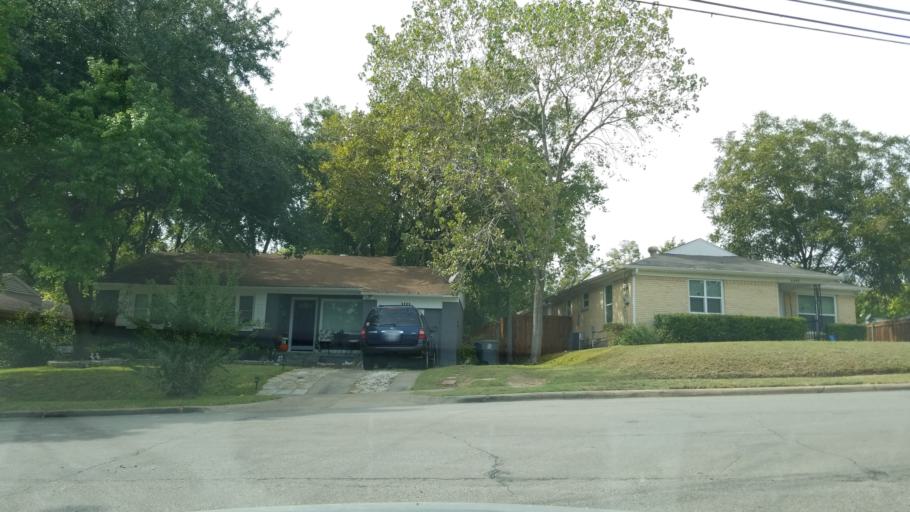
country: US
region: Texas
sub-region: Dallas County
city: Dallas
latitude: 32.7709
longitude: -96.7225
